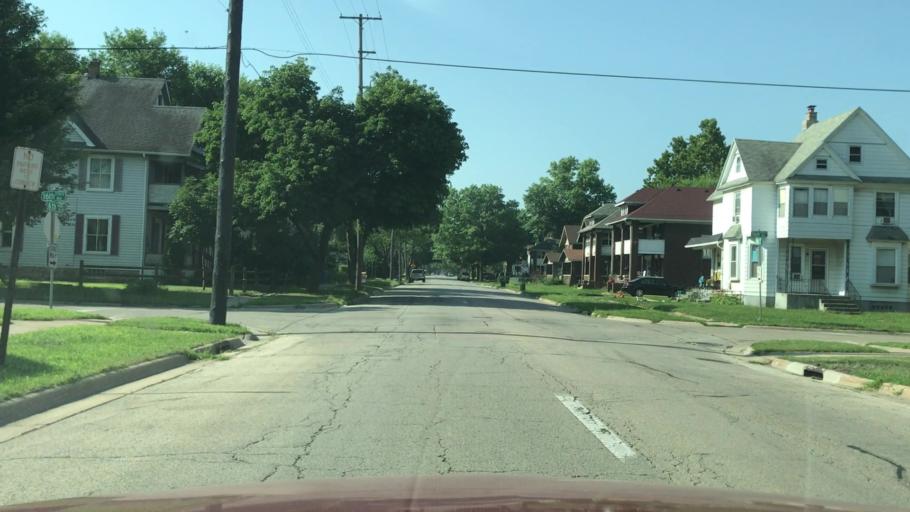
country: US
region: Illinois
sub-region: Winnebago County
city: Rockford
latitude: 42.2504
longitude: -89.0824
